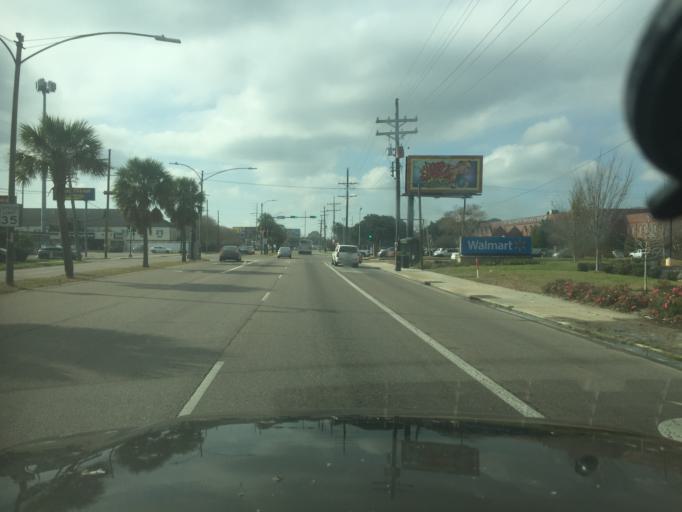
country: US
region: Louisiana
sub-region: Saint Bernard Parish
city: Arabi
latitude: 30.0043
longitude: -90.0393
